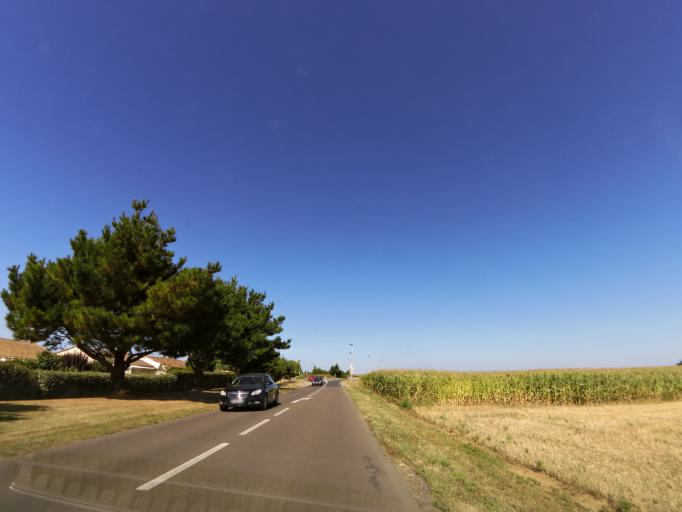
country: FR
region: Pays de la Loire
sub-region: Departement de la Vendee
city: Jard-sur-Mer
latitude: 46.4189
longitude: -1.5562
